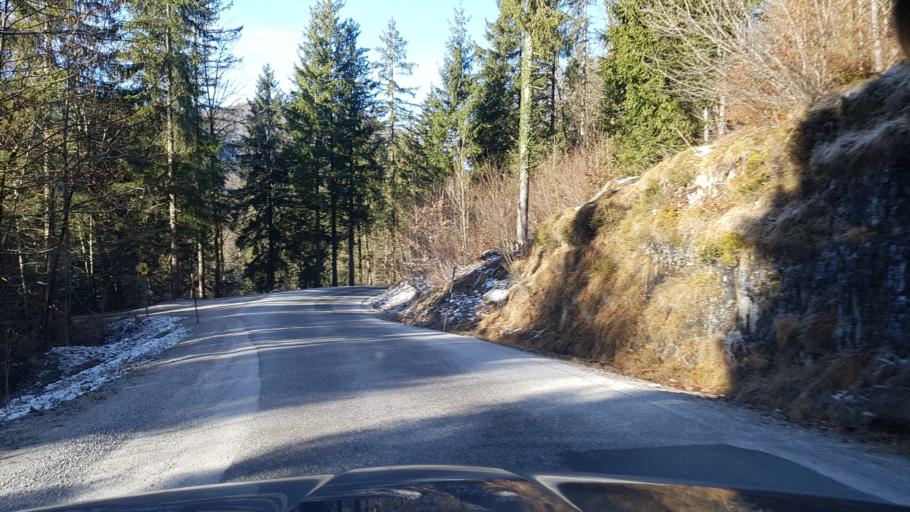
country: AT
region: Salzburg
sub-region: Politischer Bezirk Salzburg-Umgebung
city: Ebenau
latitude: 47.7743
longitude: 13.1857
